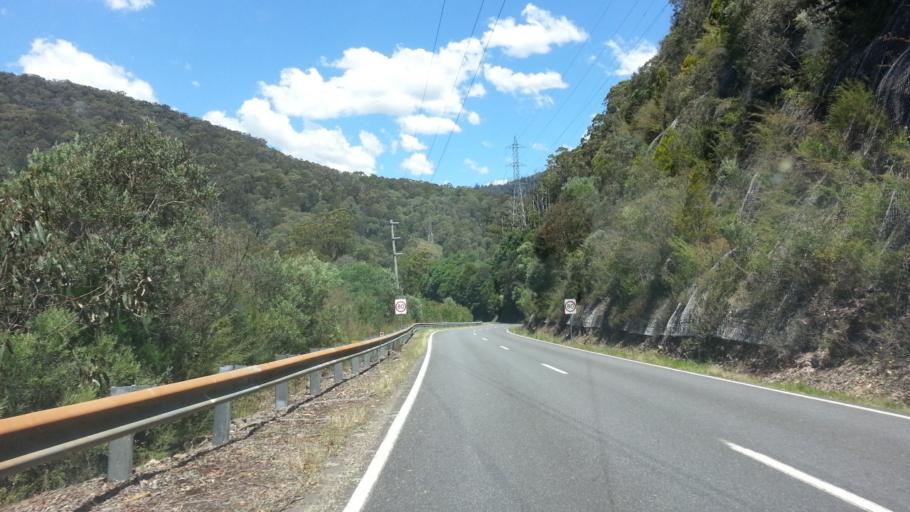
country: AU
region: Victoria
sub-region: Alpine
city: Mount Beauty
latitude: -36.7816
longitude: 147.2179
